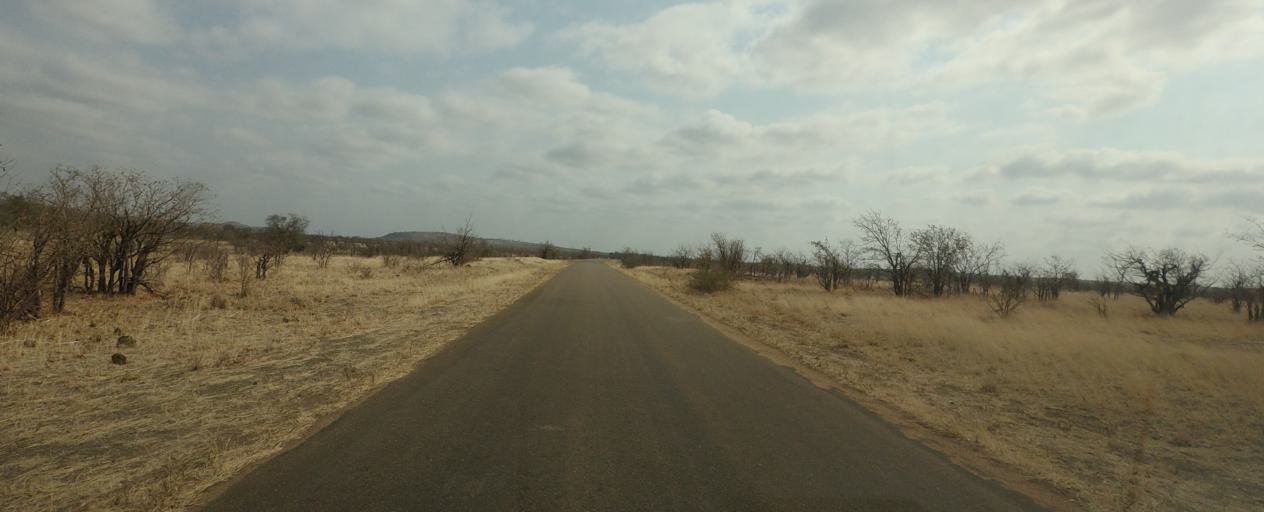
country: ZA
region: Limpopo
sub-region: Vhembe District Municipality
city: Mutale
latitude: -22.5963
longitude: 31.1792
